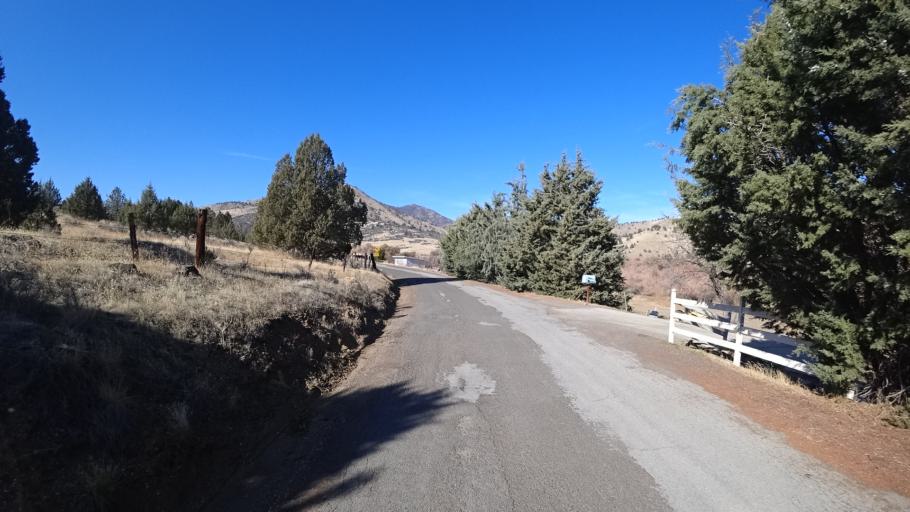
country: US
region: California
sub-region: Siskiyou County
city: Yreka
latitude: 41.7726
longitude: -122.5942
